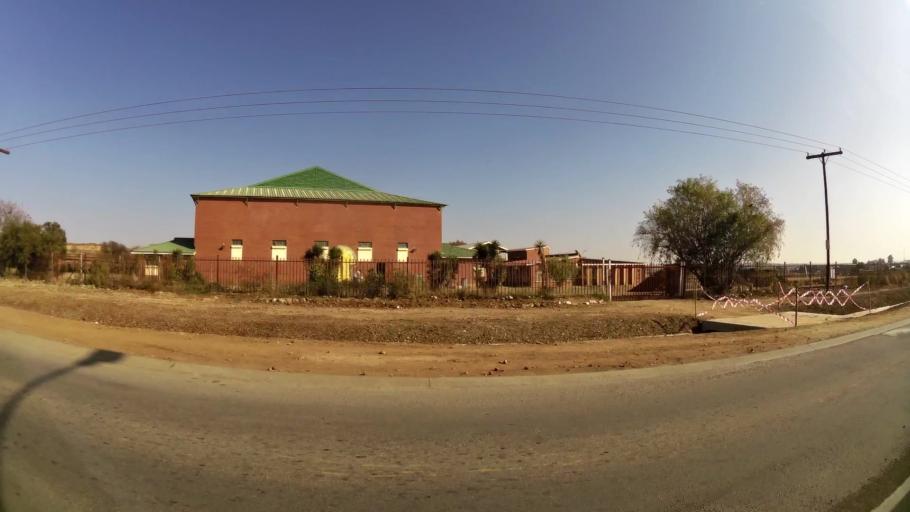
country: ZA
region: Orange Free State
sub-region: Mangaung Metropolitan Municipality
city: Bloemfontein
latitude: -29.1846
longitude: 26.2229
